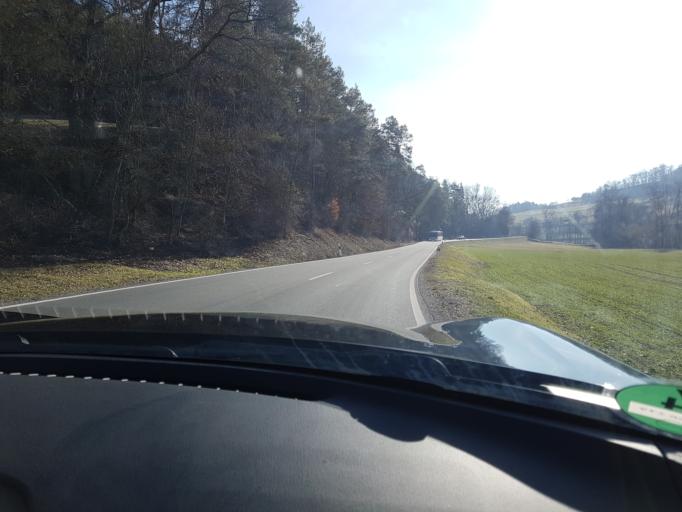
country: DE
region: Baden-Wuerttemberg
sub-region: Regierungsbezirk Stuttgart
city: Krautheim
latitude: 49.3744
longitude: 9.6554
